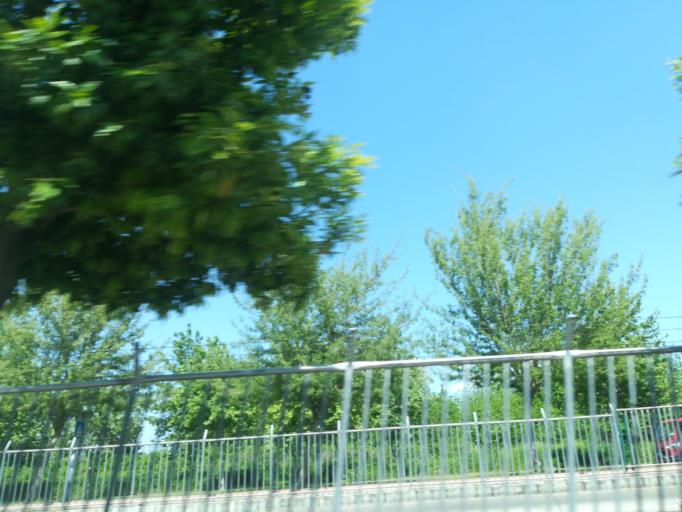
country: TR
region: Adana
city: Adana
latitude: 37.0206
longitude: 35.3720
